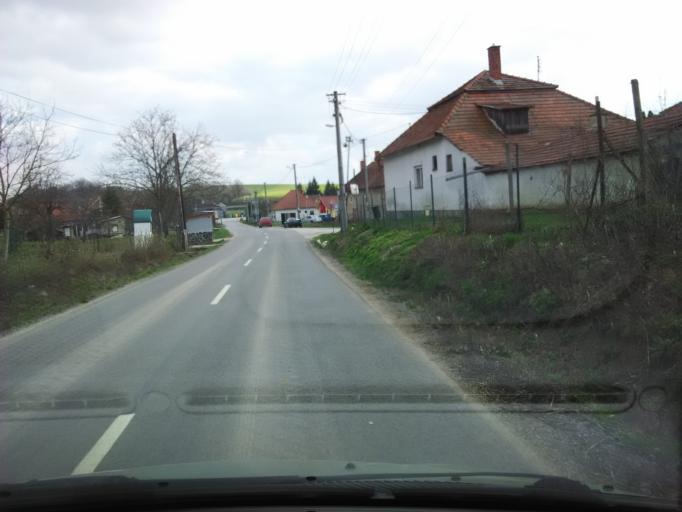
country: SK
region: Nitriansky
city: Zlate Moravce
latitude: 48.3981
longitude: 18.3259
